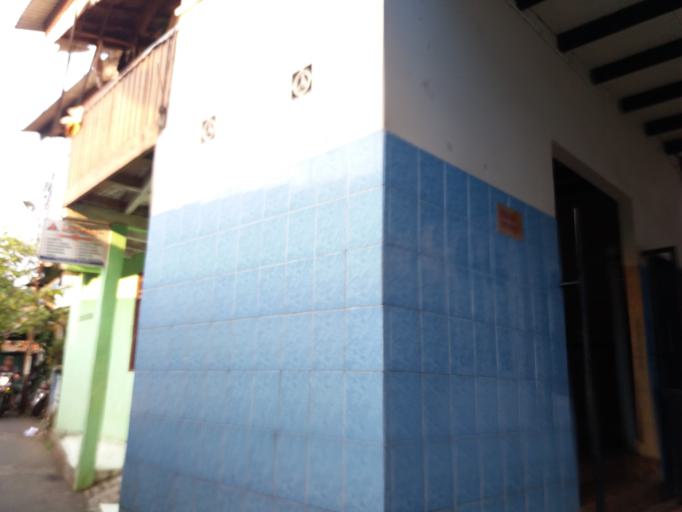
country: ID
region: Jakarta Raya
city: Jakarta
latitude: -6.2441
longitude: 106.8123
